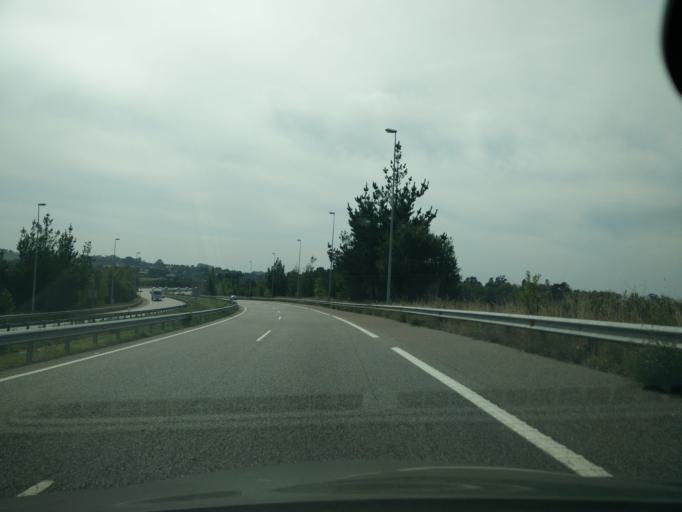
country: ES
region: Asturias
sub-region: Province of Asturias
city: Gijon
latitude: 43.5113
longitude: -5.6007
